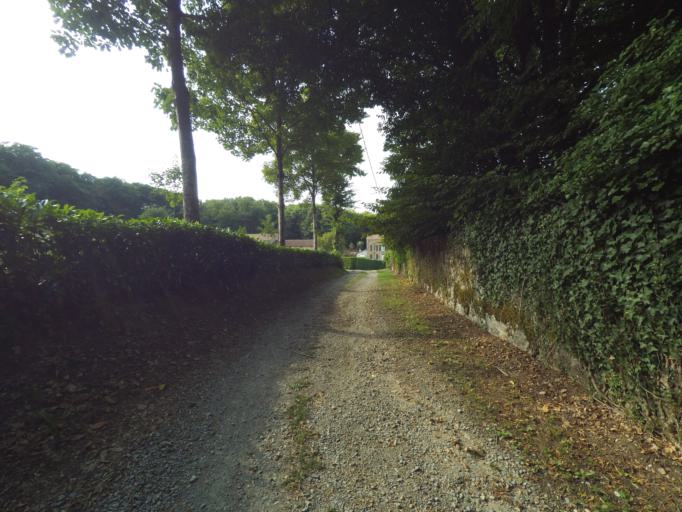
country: FR
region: Limousin
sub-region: Departement de la Haute-Vienne
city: Saint-Priest-sous-Aixe
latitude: 45.8176
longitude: 1.0651
